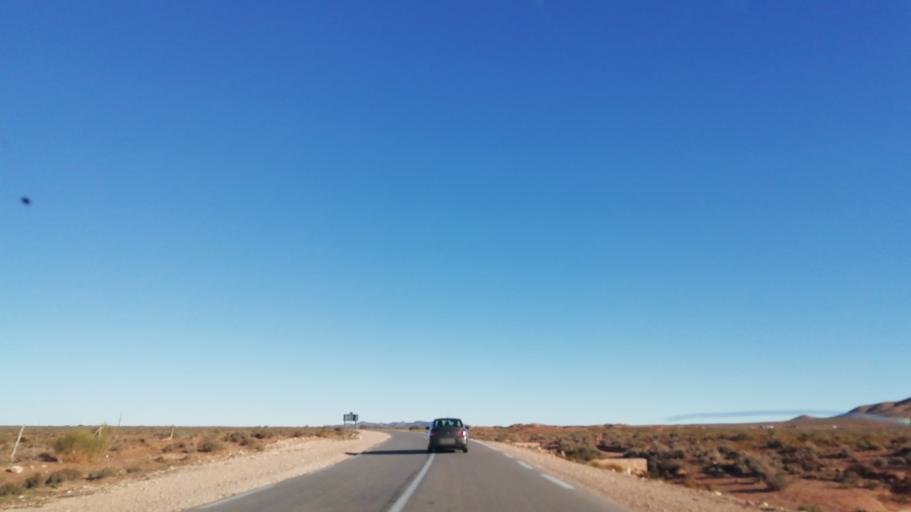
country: DZ
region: El Bayadh
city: El Abiodh Sidi Cheikh
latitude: 33.1122
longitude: 0.2526
